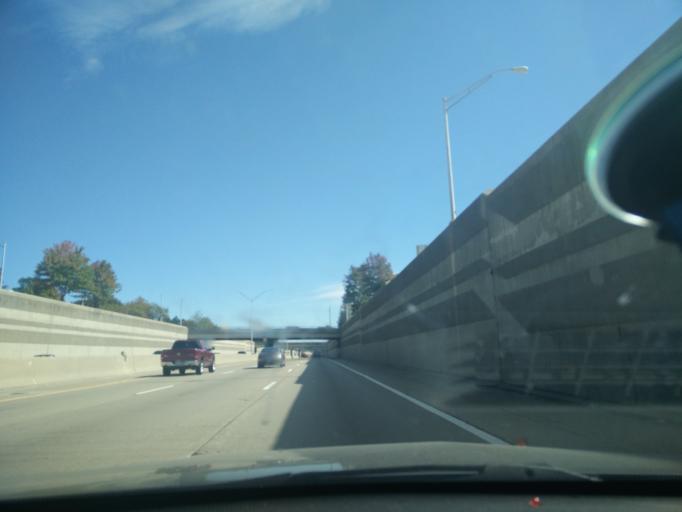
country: US
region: Michigan
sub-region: Oakland County
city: Lathrup Village
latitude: 42.4870
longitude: -83.2466
